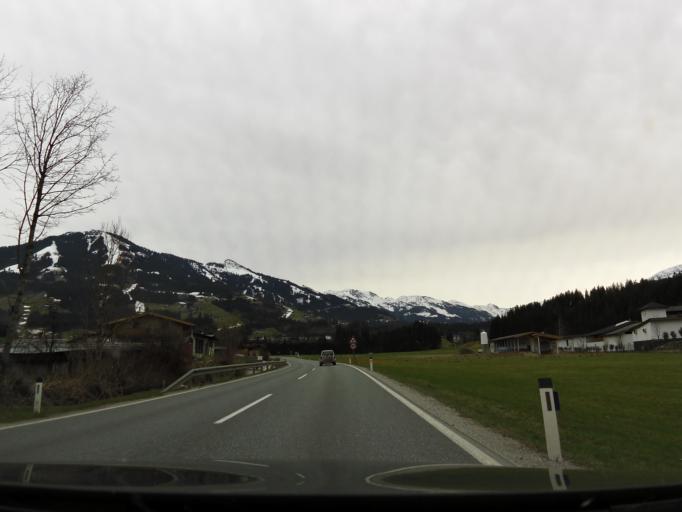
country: AT
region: Tyrol
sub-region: Politischer Bezirk Kitzbuhel
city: Westendorf
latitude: 47.4367
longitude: 12.1929
